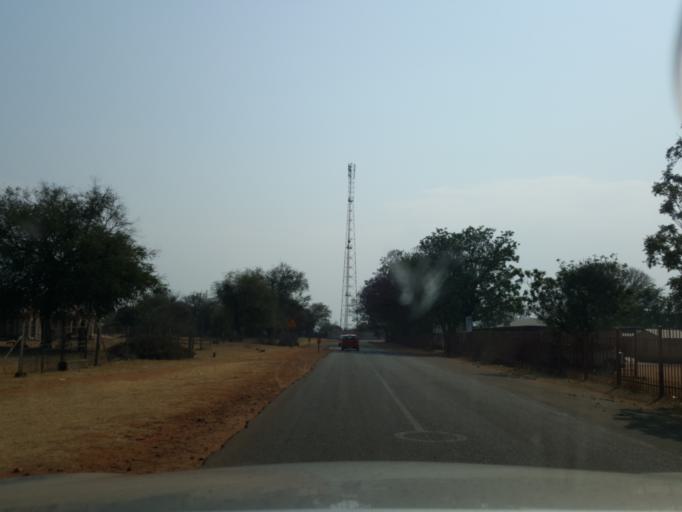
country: BW
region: South East
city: Lobatse
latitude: -25.2856
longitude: 25.9131
